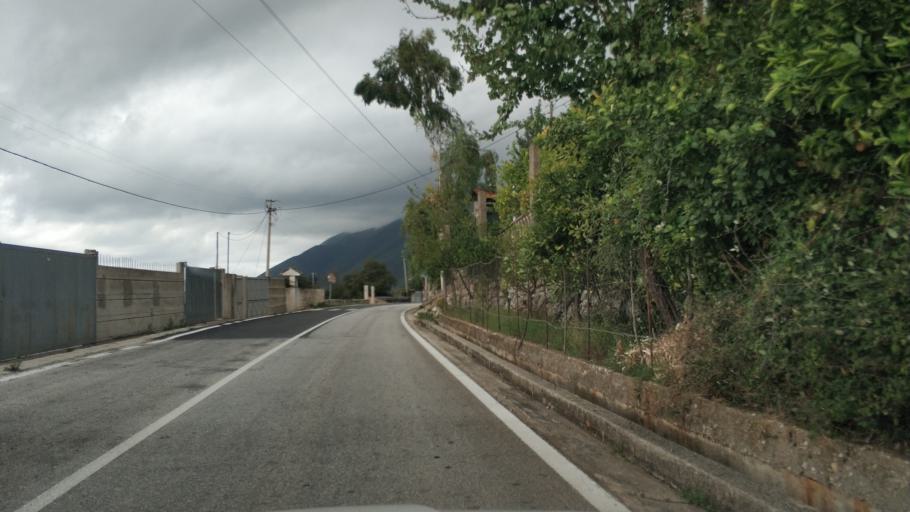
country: AL
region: Vlore
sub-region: Rrethi i Vlores
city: Vranisht
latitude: 40.1632
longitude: 19.6221
